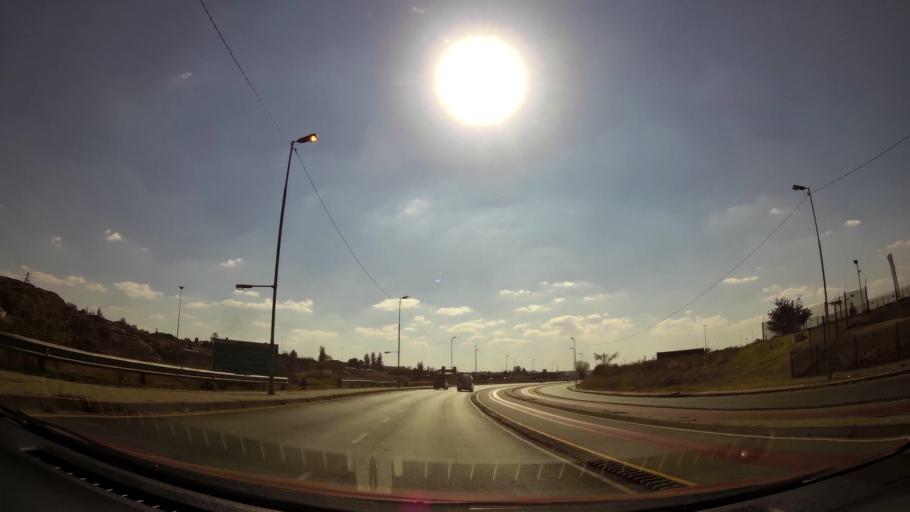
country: ZA
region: Gauteng
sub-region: City of Johannesburg Metropolitan Municipality
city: Soweto
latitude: -26.2432
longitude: 27.9108
